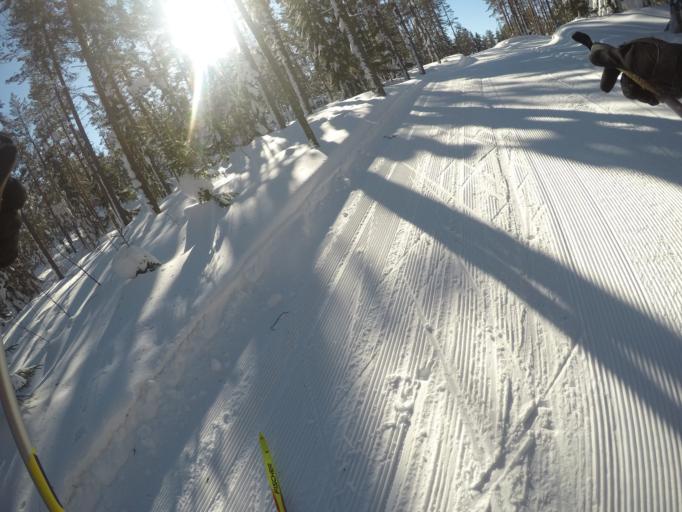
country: SE
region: Vaesternorrland
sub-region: Sundsvalls Kommun
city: Sundsvall
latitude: 62.3679
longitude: 17.2953
